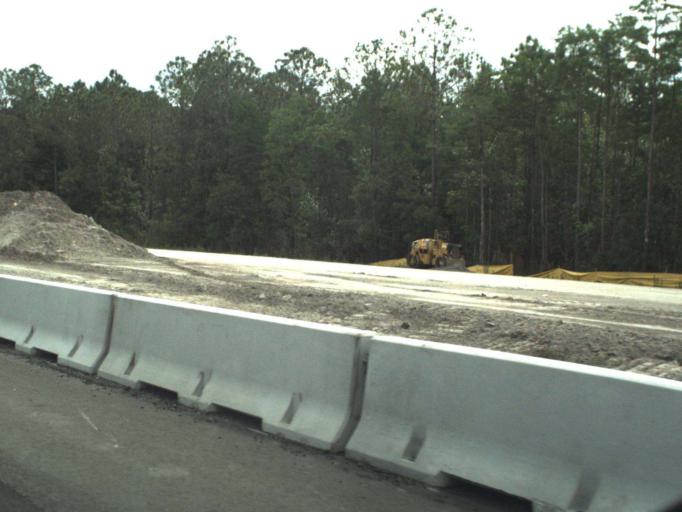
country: US
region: Florida
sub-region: Volusia County
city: Lake Helen
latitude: 29.0732
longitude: -81.1791
